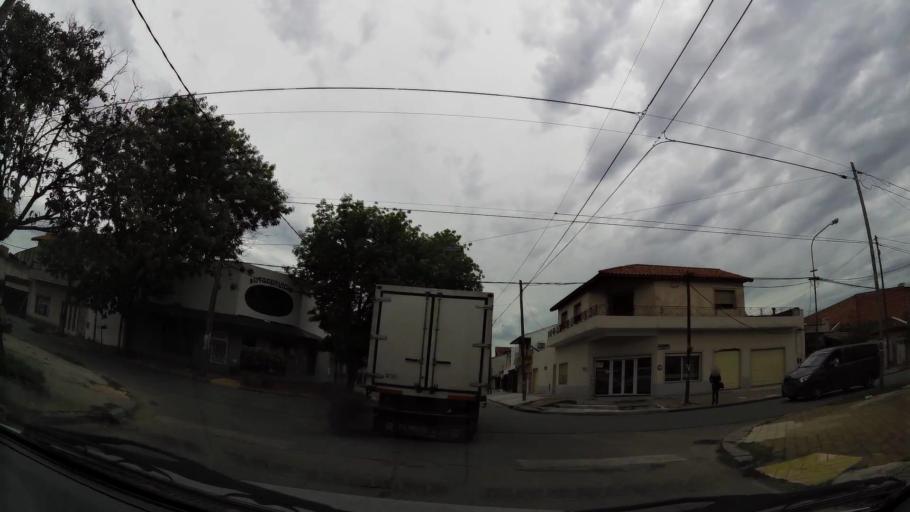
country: AR
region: Buenos Aires
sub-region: Partido de Lanus
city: Lanus
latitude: -34.6853
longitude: -58.3933
